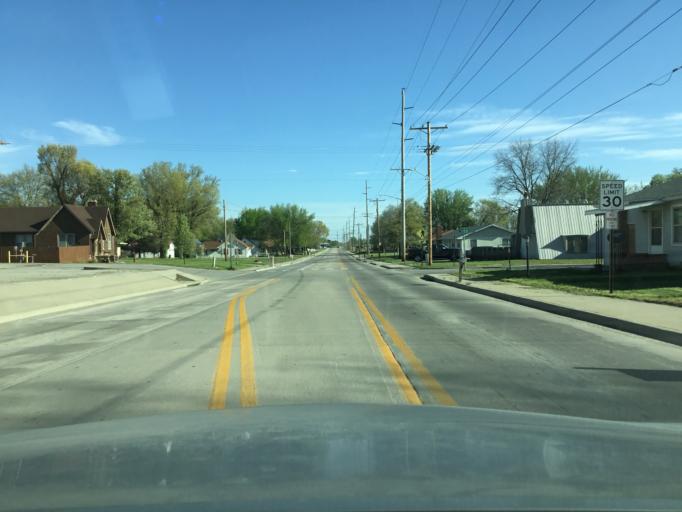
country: US
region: Kansas
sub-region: Neosho County
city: Chanute
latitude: 37.6825
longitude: -95.4708
